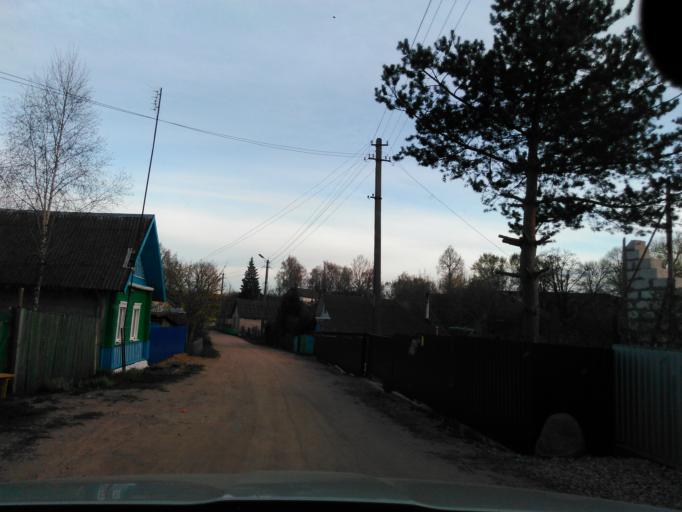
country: BY
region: Vitebsk
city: Chashniki
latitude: 54.8618
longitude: 29.1661
